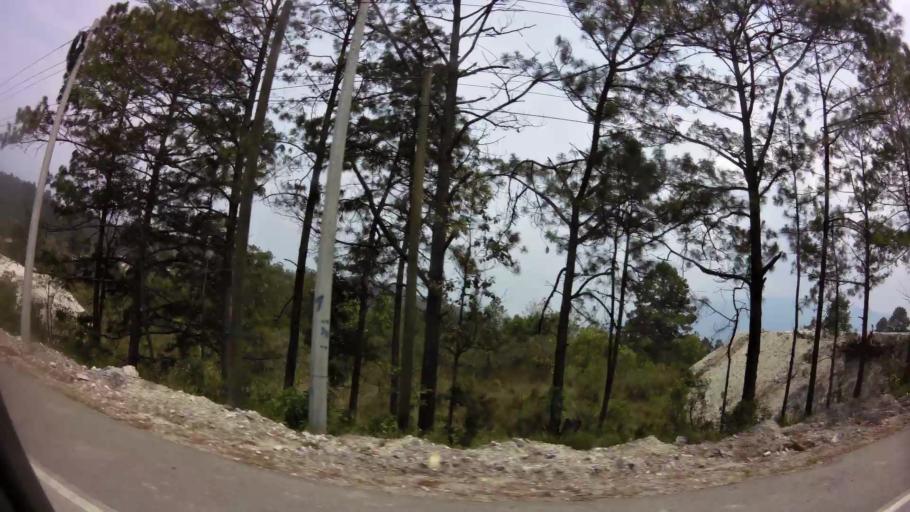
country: HN
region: Comayagua
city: El Socorro
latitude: 14.6475
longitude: -87.9316
